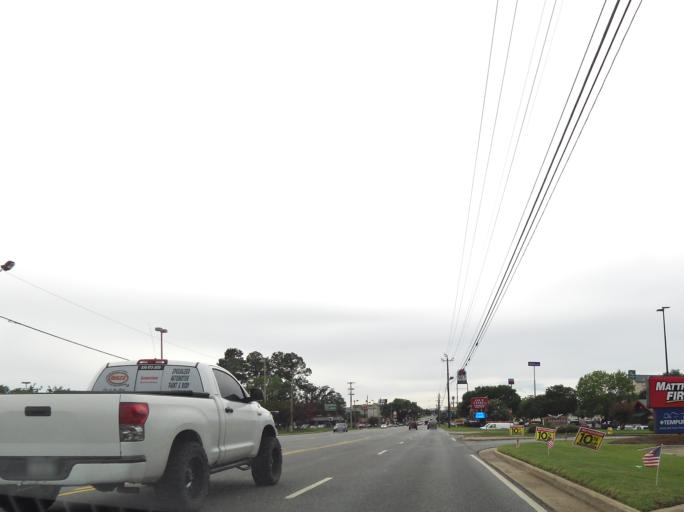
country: US
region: Georgia
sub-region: Lowndes County
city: Remerton
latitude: 30.8407
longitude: -83.3220
